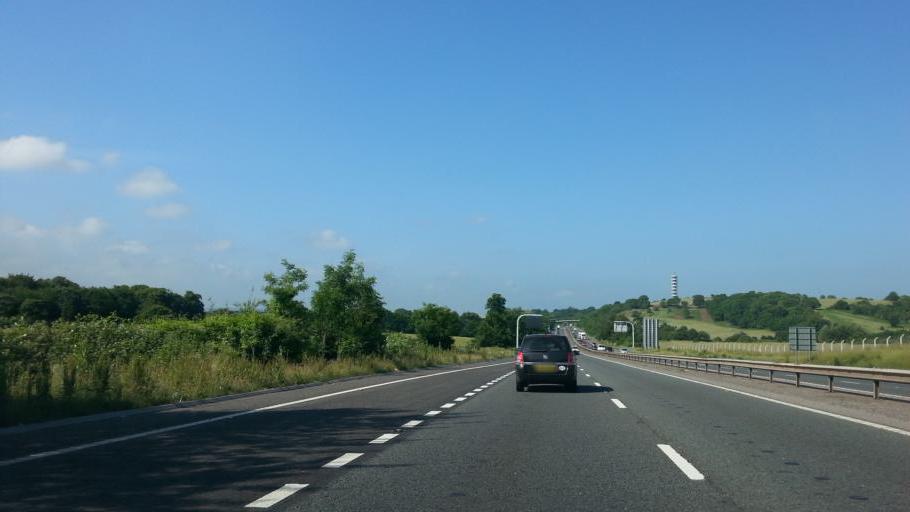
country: GB
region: England
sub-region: South Gloucestershire
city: Stoke Gifford
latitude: 51.4917
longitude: -2.5434
